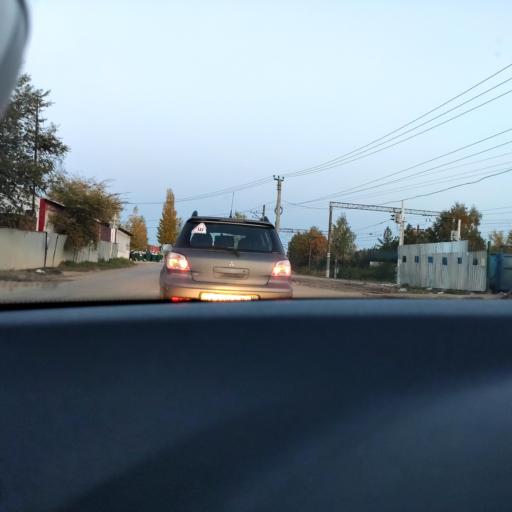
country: RU
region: Samara
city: Novosemeykino
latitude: 53.3695
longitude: 50.3541
